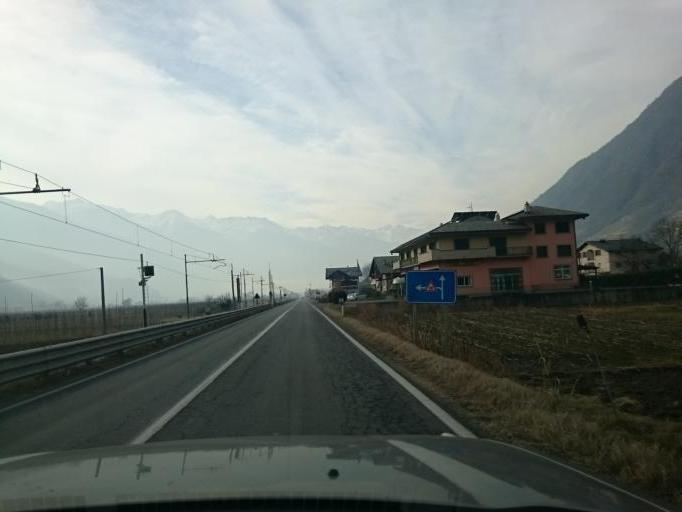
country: IT
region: Lombardy
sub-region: Provincia di Sondrio
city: Villa
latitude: 46.2075
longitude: 10.1432
